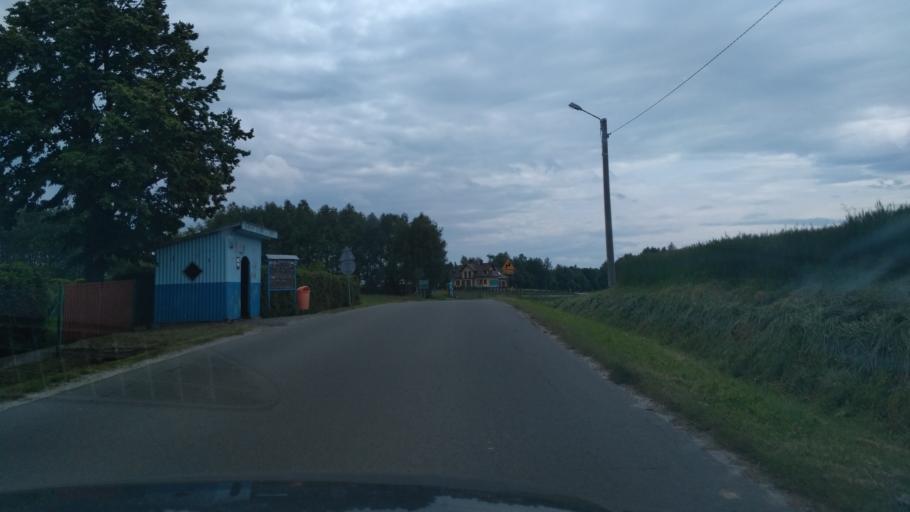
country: PL
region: Subcarpathian Voivodeship
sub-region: Powiat ropczycko-sedziszowski
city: Wielopole Skrzynskie
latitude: 49.9774
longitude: 21.6262
